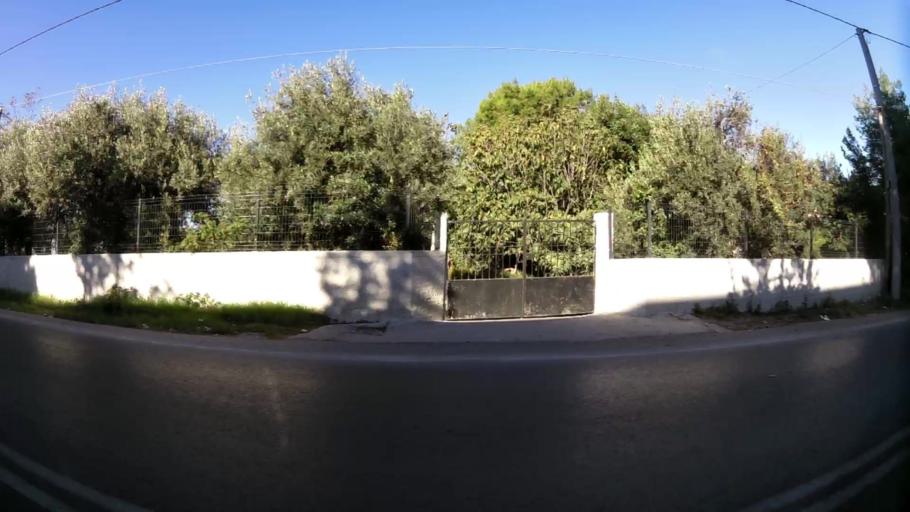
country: GR
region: Attica
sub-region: Nomarchia Athinas
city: Metamorfosi
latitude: 38.0744
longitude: 23.7605
